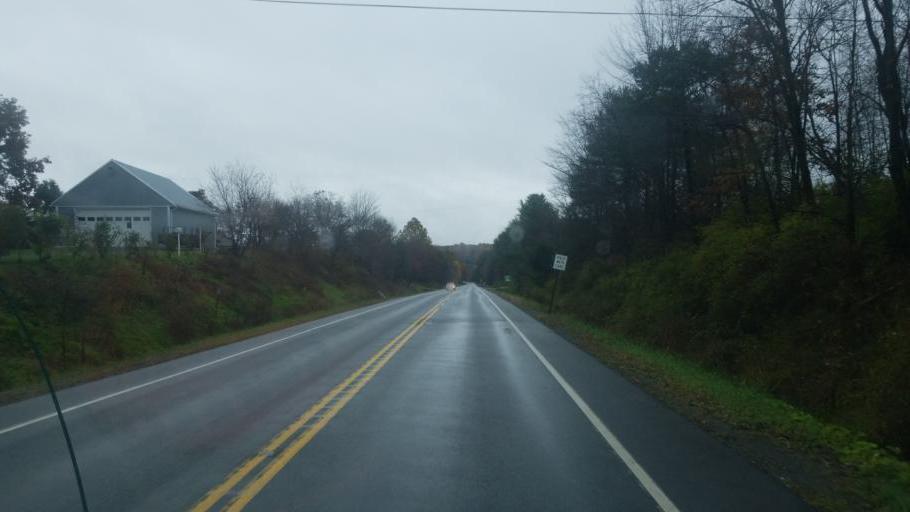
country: US
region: Pennsylvania
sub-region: Clearfield County
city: Shiloh
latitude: 41.1029
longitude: -78.2200
